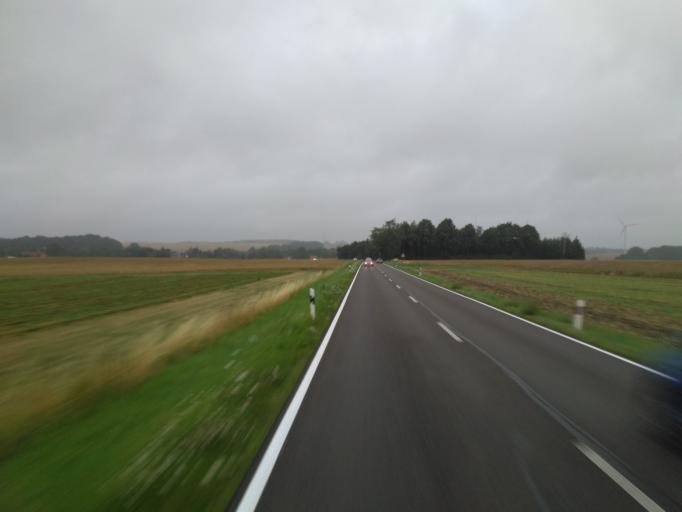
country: DE
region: Saxony
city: Nossen
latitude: 51.0697
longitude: 13.3407
